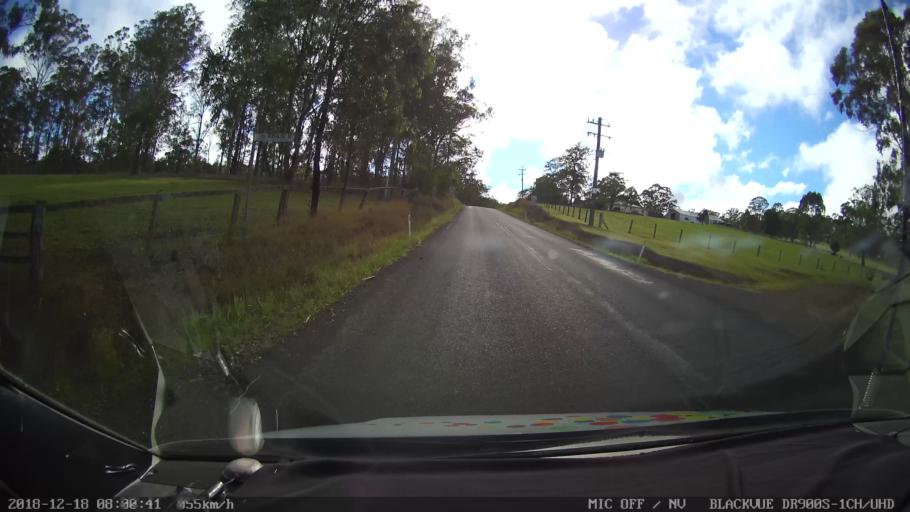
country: AU
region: New South Wales
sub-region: Kyogle
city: Kyogle
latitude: -28.3892
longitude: 152.6148
